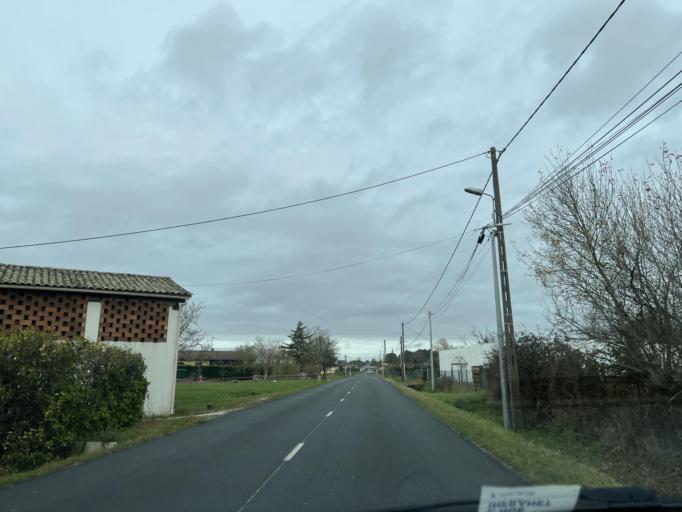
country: FR
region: Aquitaine
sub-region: Departement de la Gironde
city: Saint-Ciers-sur-Gironde
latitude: 45.2787
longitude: -0.6131
